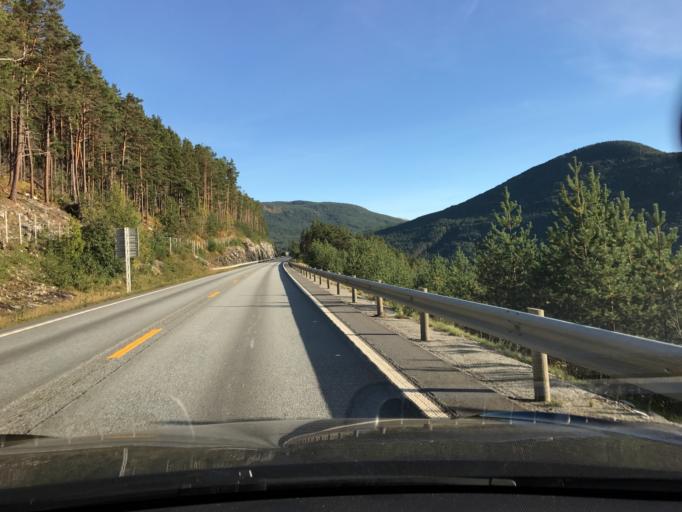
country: NO
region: Sogn og Fjordane
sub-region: Sogndal
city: Sogndalsfjora
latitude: 61.1858
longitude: 7.2535
